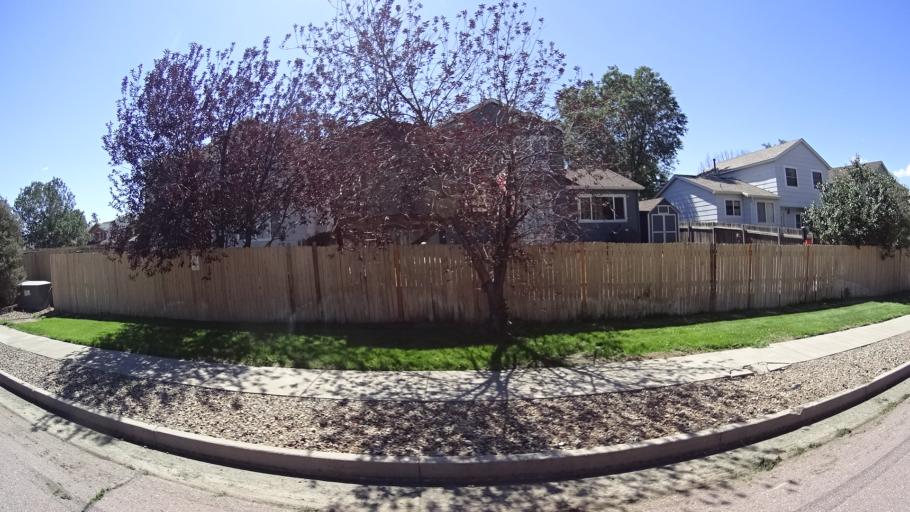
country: US
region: Colorado
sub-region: El Paso County
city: Security-Widefield
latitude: 38.7676
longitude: -104.6543
